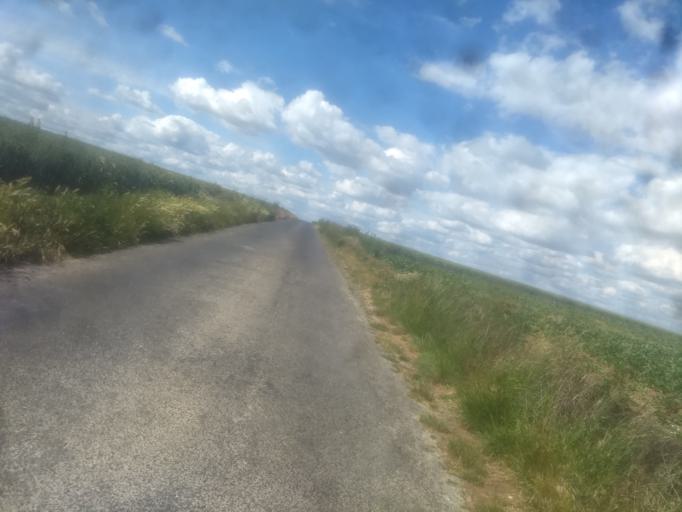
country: FR
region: Nord-Pas-de-Calais
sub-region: Departement du Pas-de-Calais
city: Tilloy-les-Mofflaines
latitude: 50.2627
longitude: 2.8188
